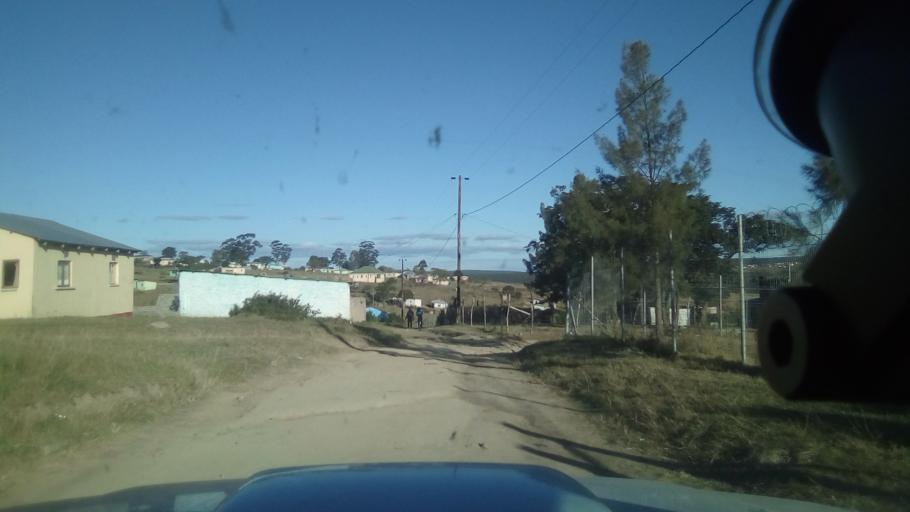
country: ZA
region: Eastern Cape
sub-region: Buffalo City Metropolitan Municipality
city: Bhisho
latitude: -32.7337
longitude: 27.3610
